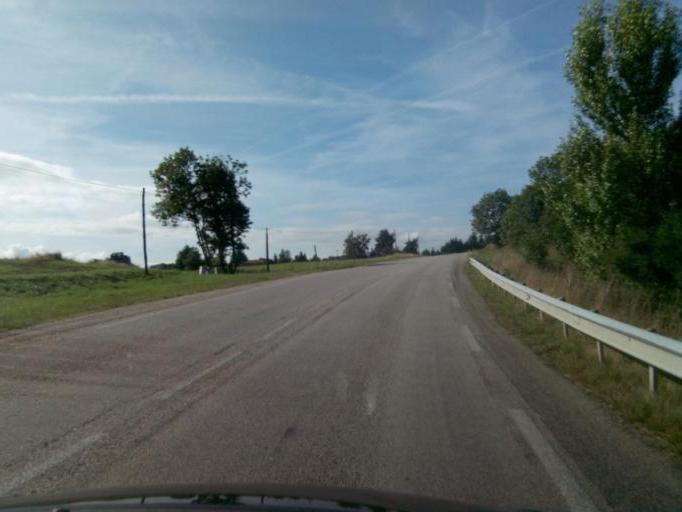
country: FR
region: Auvergne
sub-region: Departement de la Haute-Loire
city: Beauzac
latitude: 45.2797
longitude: 4.1115
